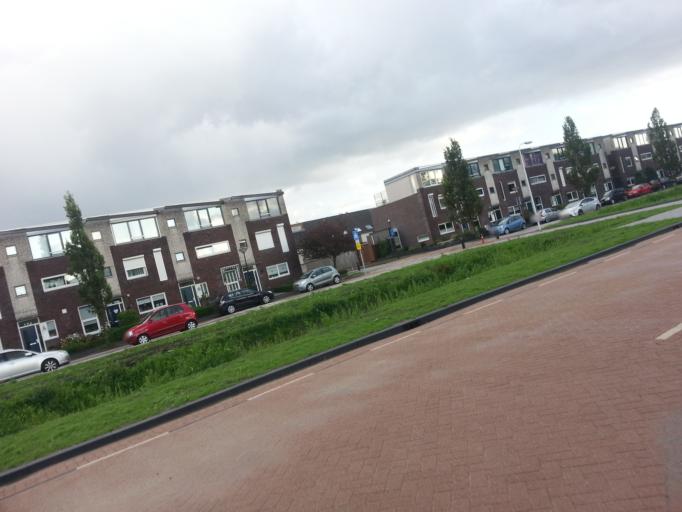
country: NL
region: South Holland
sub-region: Gemeente Spijkenisse
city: Spijkenisse
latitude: 51.8266
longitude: 4.2531
